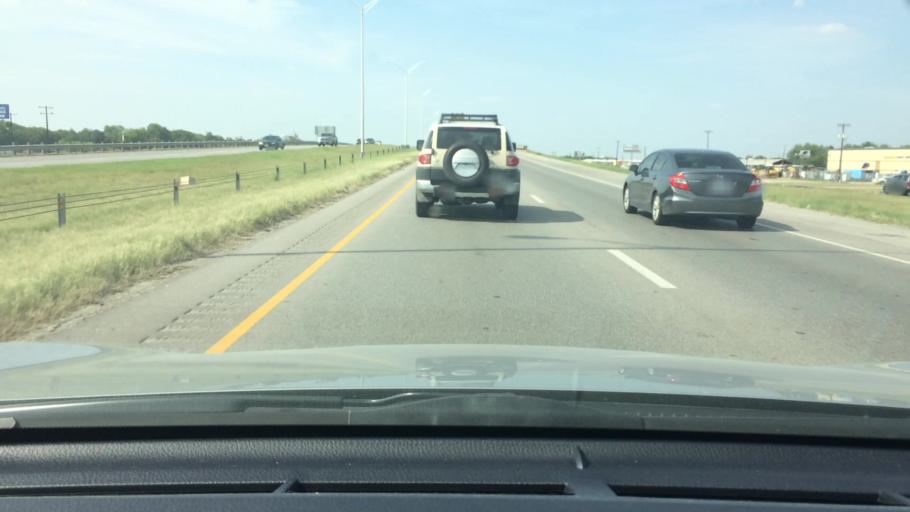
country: US
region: Texas
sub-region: Bexar County
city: China Grove
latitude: 29.3844
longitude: -98.3909
